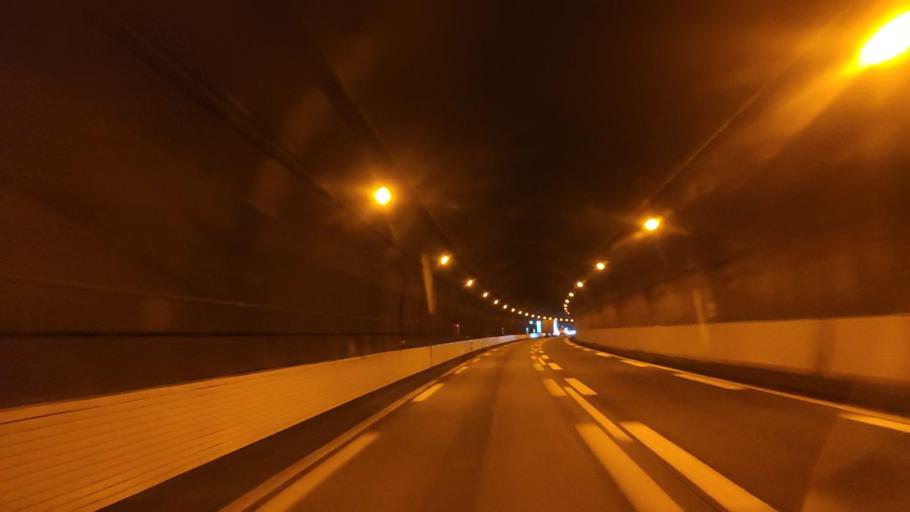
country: JP
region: Niigata
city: Joetsu
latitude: 37.1663
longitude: 138.1004
